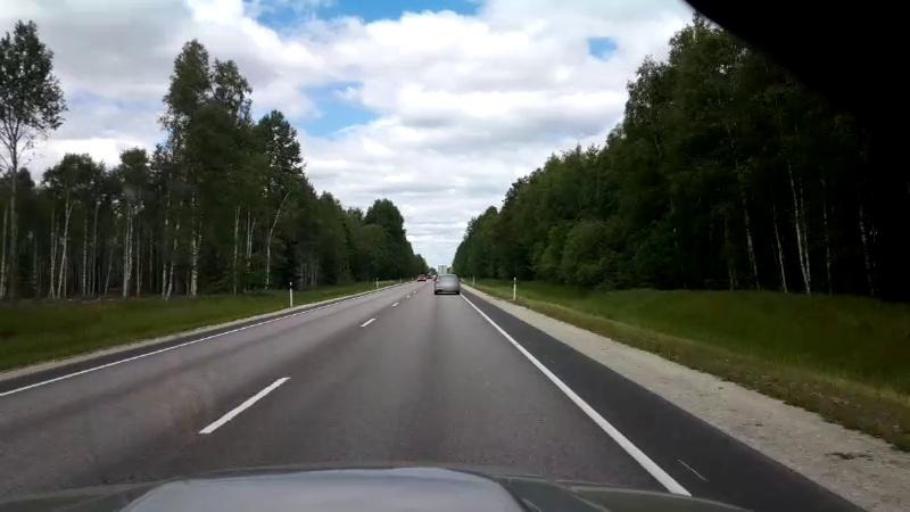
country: EE
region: Paernumaa
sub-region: Halinga vald
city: Parnu-Jaagupi
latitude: 58.7286
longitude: 24.4236
